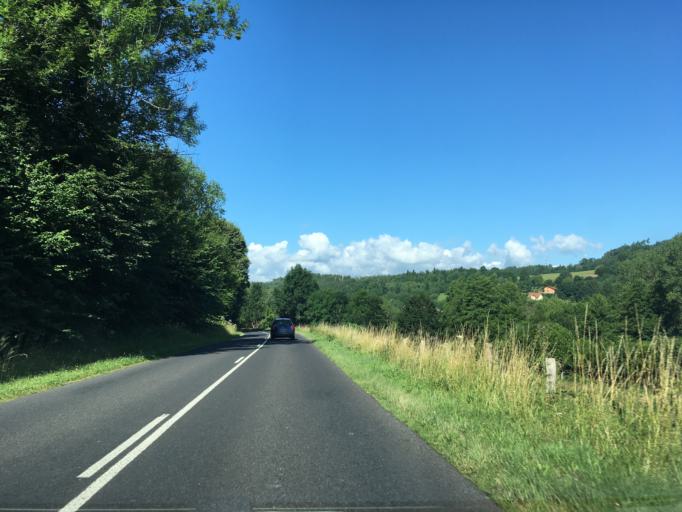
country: FR
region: Lorraine
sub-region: Departement des Vosges
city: Ban-de-Laveline
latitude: 48.2548
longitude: 7.0898
